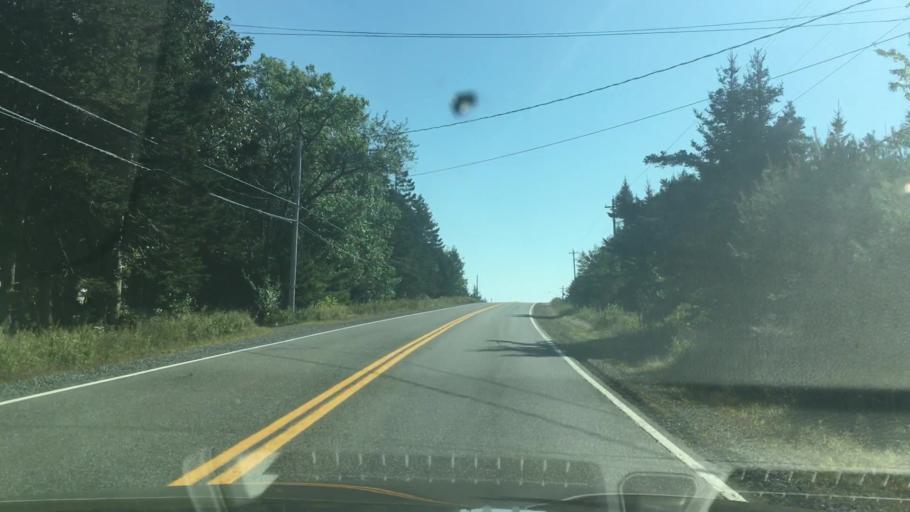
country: CA
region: Nova Scotia
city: Cole Harbour
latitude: 44.7795
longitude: -63.0017
